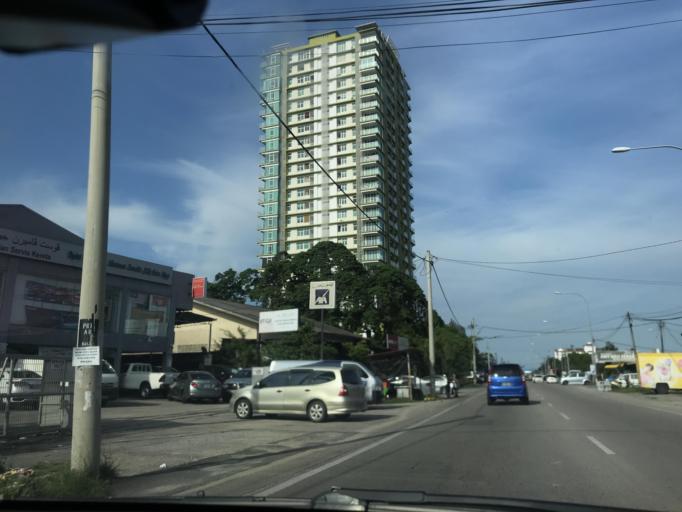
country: MY
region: Kelantan
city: Kota Bharu
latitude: 6.1243
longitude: 102.2682
